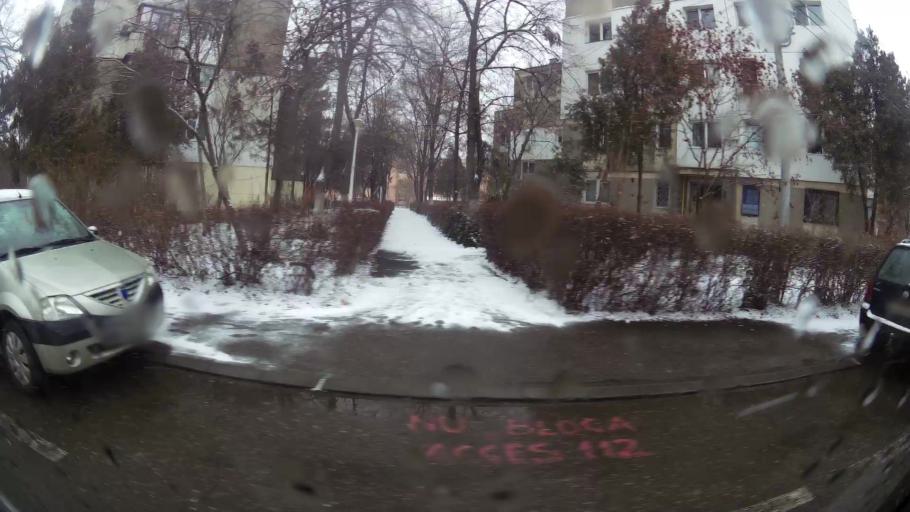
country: RO
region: Prahova
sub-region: Comuna Targsoru Vechi
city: Strejnicu
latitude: 44.9337
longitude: 25.9825
